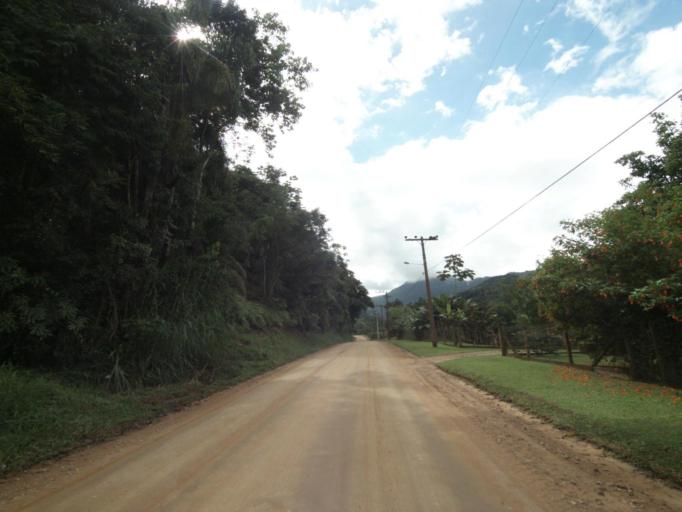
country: BR
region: Santa Catarina
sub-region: Pomerode
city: Pomerode
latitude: -26.7145
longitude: -49.2082
